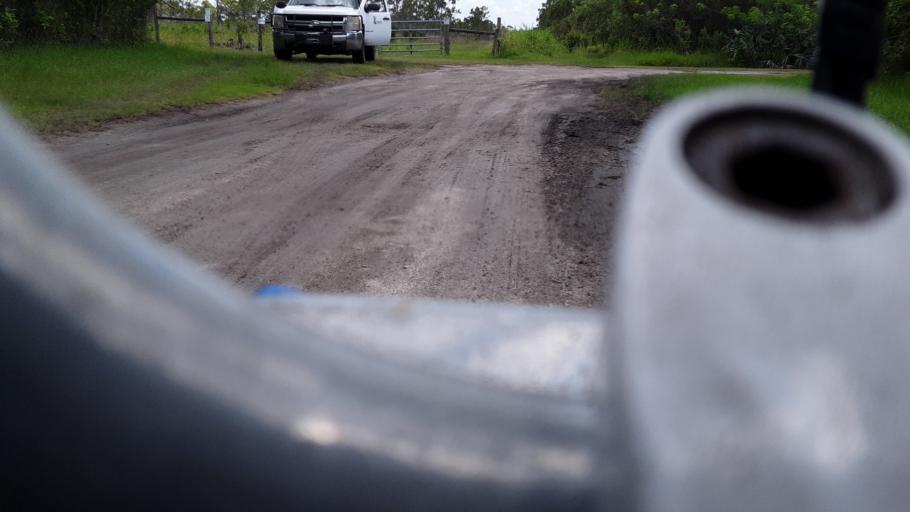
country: US
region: Florida
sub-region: Brevard County
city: Malabar
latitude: 27.9852
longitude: -80.5733
